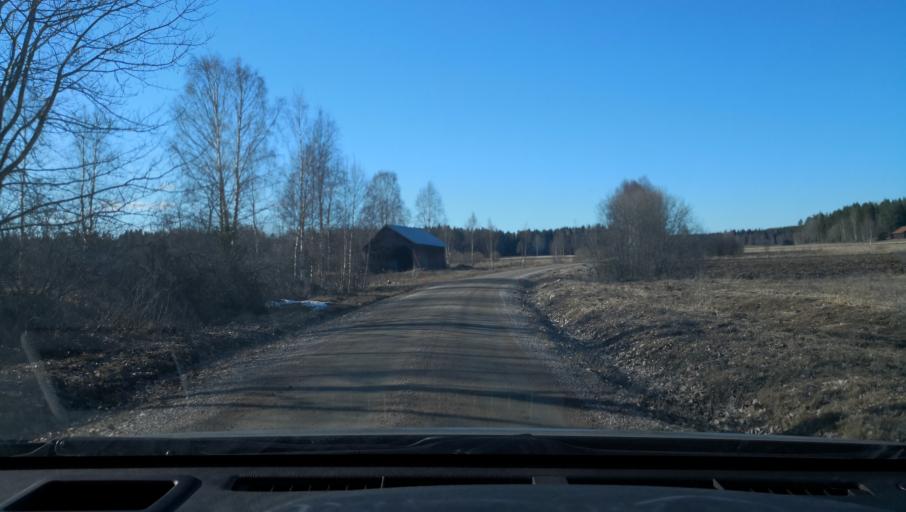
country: SE
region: Vaestmanland
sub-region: Sala Kommun
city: Sala
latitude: 60.1231
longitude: 16.6578
